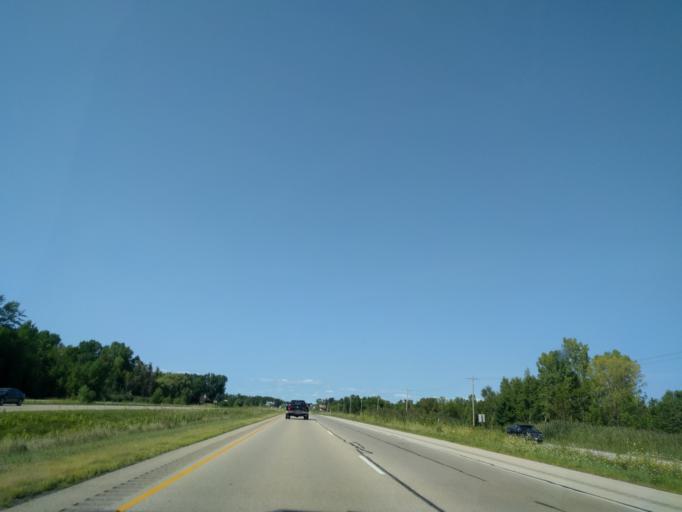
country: US
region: Wisconsin
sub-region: Brown County
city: Suamico
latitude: 44.6904
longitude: -88.0504
